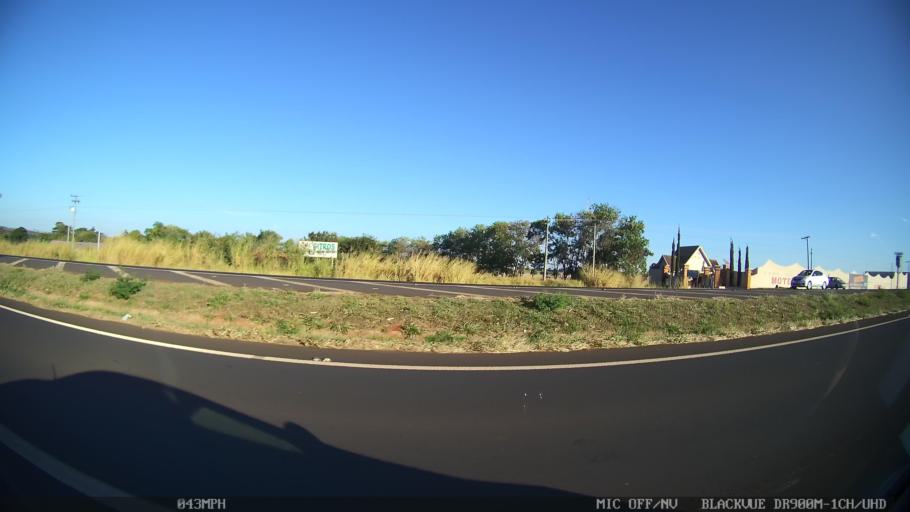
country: BR
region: Sao Paulo
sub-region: Guapiacu
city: Guapiacu
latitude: -20.7712
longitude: -49.2188
